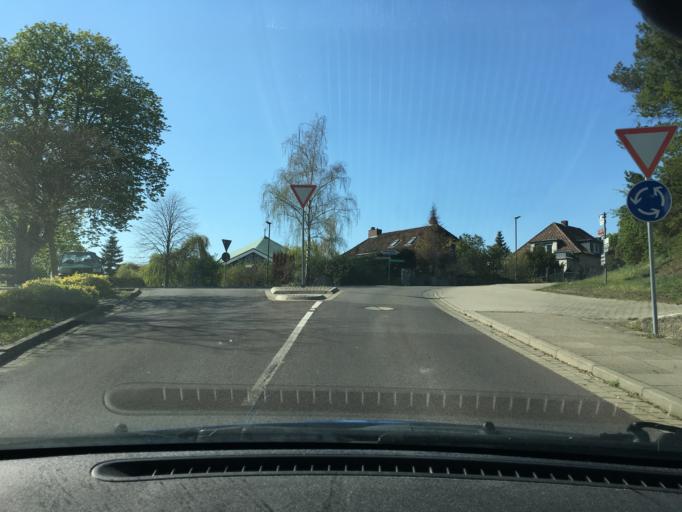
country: DE
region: Lower Saxony
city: Hitzacker
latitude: 53.1503
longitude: 11.0432
